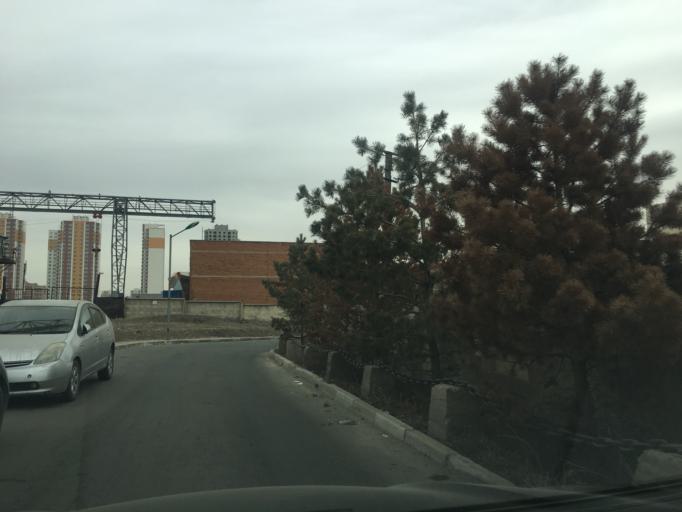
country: MN
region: Ulaanbaatar
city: Ulaanbaatar
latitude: 47.9044
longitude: 106.8893
